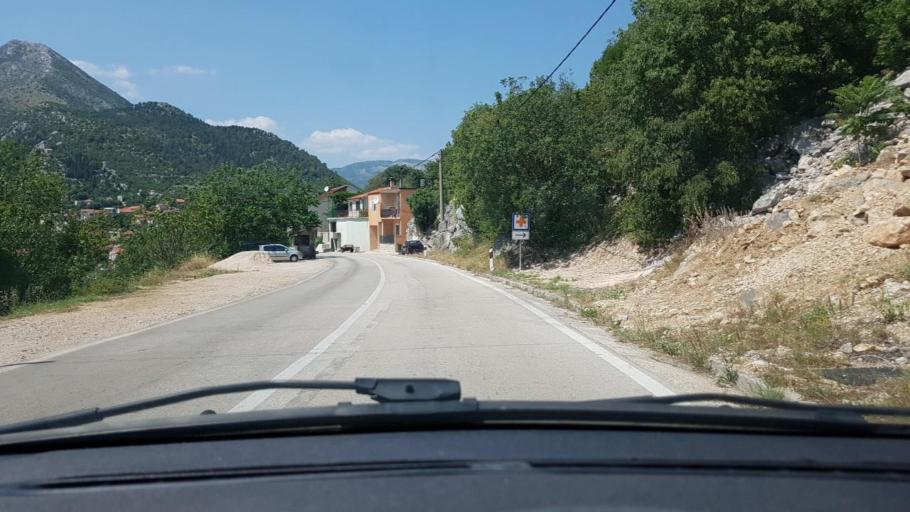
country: HR
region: Splitsko-Dalmatinska
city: Vrgorac
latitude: 43.2001
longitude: 17.3770
